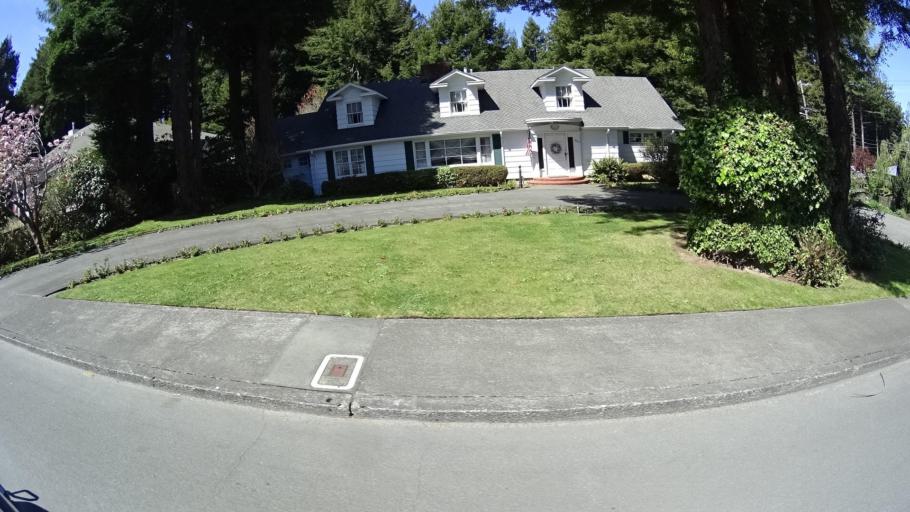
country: US
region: California
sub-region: Humboldt County
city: Myrtletown
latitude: 40.7876
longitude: -124.1491
